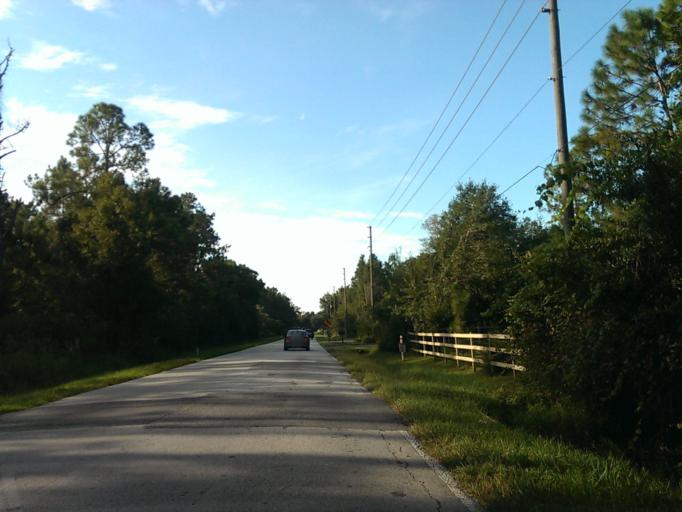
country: US
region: Florida
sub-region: Orange County
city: Lake Butler
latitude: 28.4526
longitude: -81.5961
